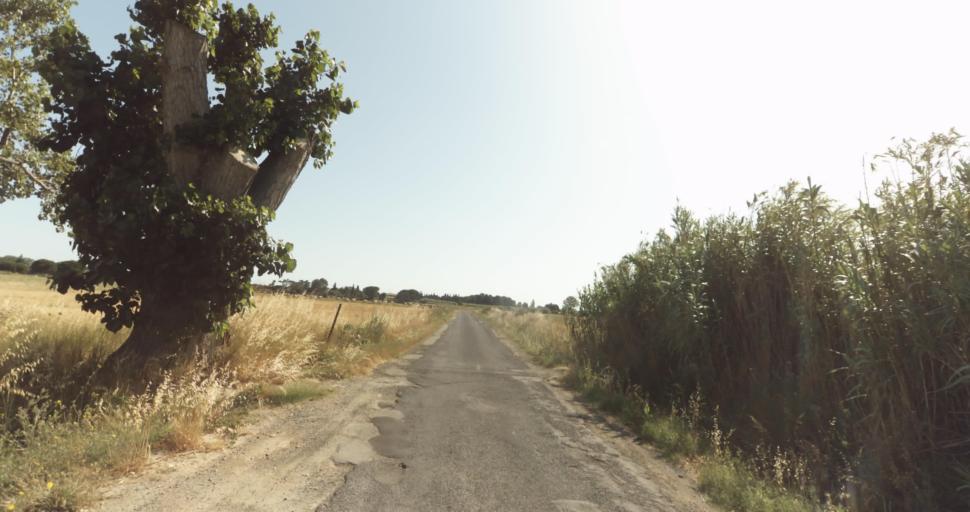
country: FR
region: Languedoc-Roussillon
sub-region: Departement des Pyrenees-Orientales
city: Alenya
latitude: 42.6336
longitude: 3.0007
